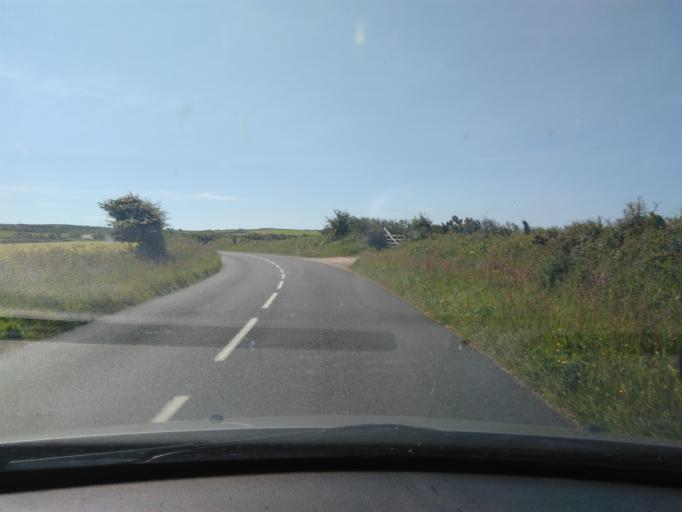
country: FR
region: Lower Normandy
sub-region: Departement de la Manche
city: Beaumont-Hague
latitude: 49.7037
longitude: -1.9303
